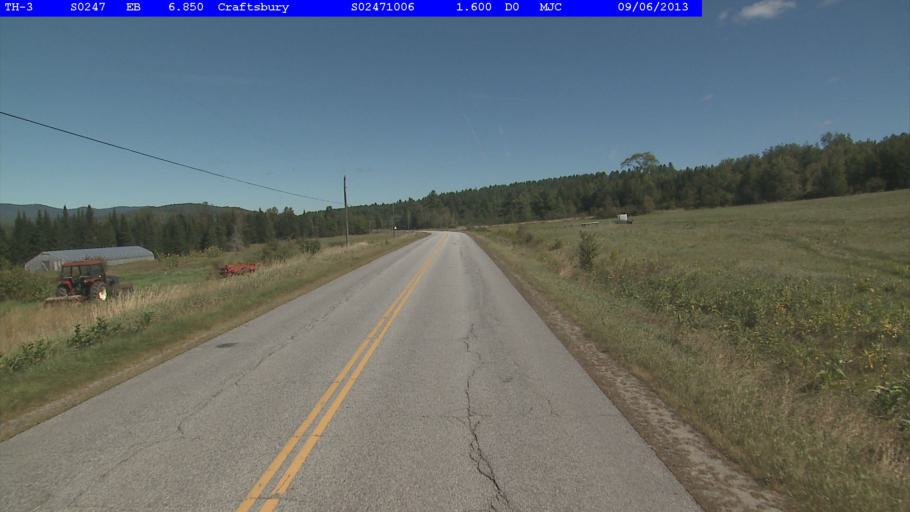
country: US
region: Vermont
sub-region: Caledonia County
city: Hardwick
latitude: 44.6347
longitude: -72.4212
